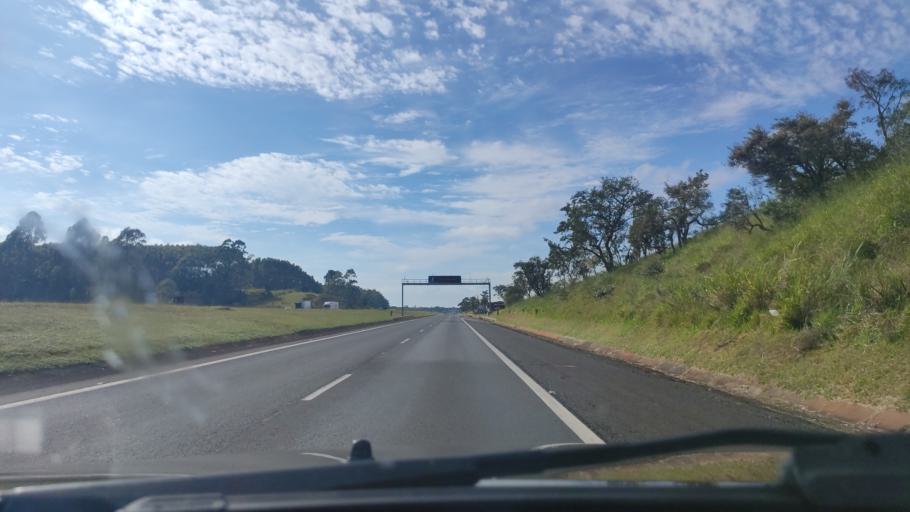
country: BR
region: Sao Paulo
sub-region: Itatinga
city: Itatinga
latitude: -23.0697
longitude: -48.5442
